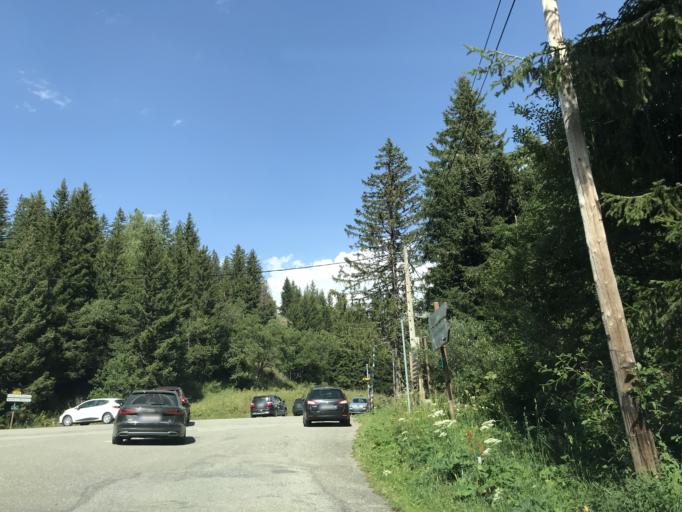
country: FR
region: Rhone-Alpes
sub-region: Departement de la Savoie
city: Beaufort
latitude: 45.6946
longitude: 6.6333
